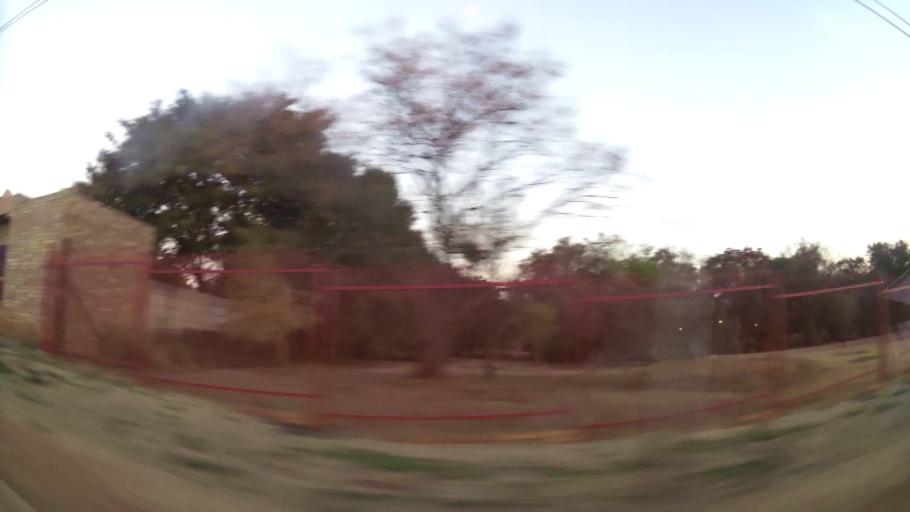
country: ZA
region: Gauteng
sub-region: City of Tshwane Metropolitan Municipality
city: Centurion
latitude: -25.8448
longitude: 28.1246
